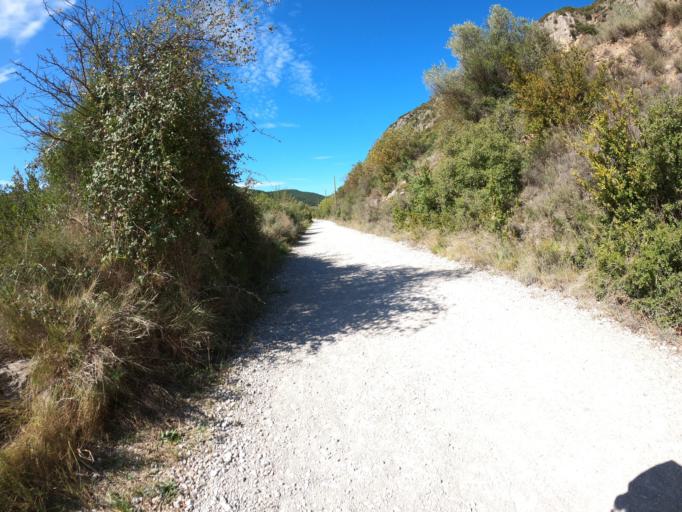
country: ES
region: Navarre
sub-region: Provincia de Navarra
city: Liedena
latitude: 42.6242
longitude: -1.2956
